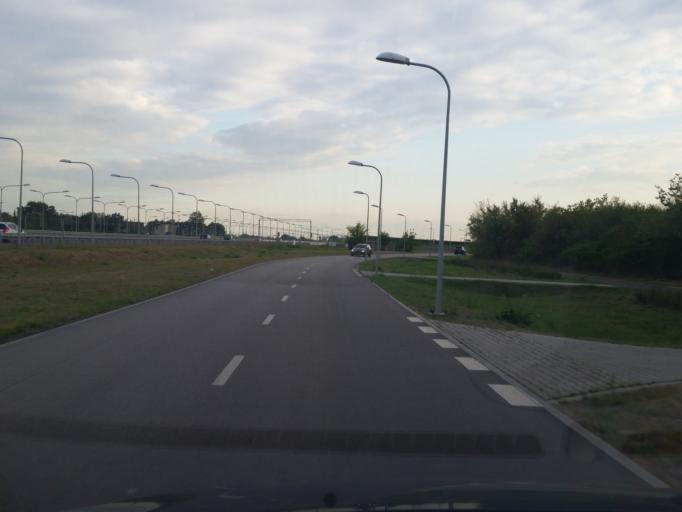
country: PL
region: Masovian Voivodeship
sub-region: Powiat piaseczynski
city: Mysiadlo
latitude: 52.1434
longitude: 20.9882
